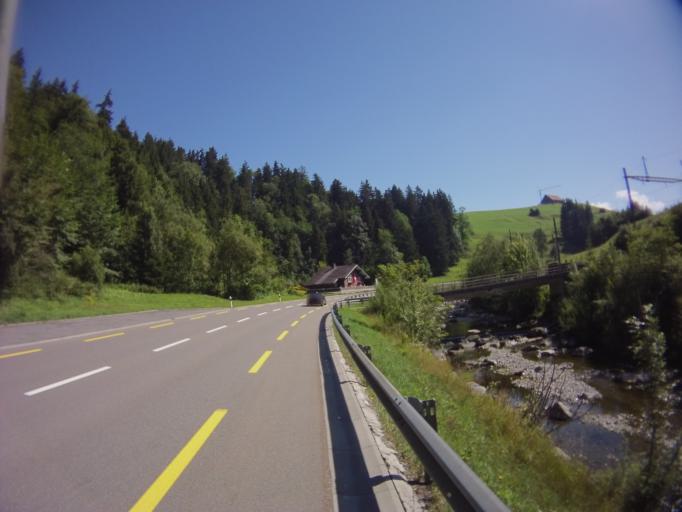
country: CH
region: Schwyz
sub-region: Bezirk Einsiedeln
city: Einsiedeln
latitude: 47.1522
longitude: 8.7433
